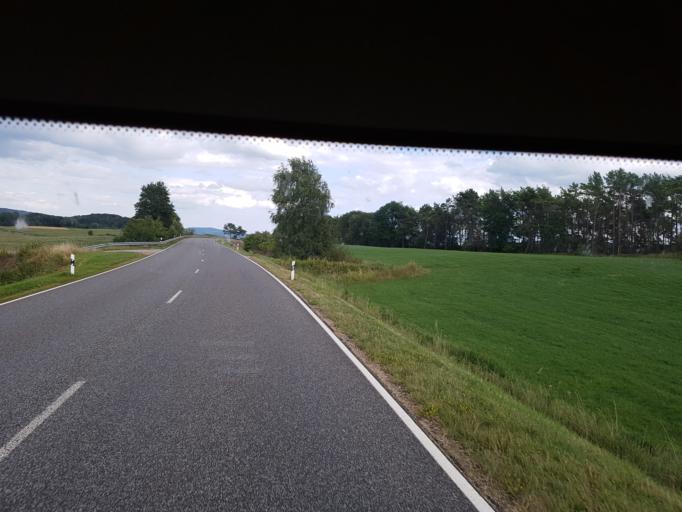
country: DE
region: Rheinland-Pfalz
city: Schwirzheim
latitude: 50.2171
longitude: 6.5276
